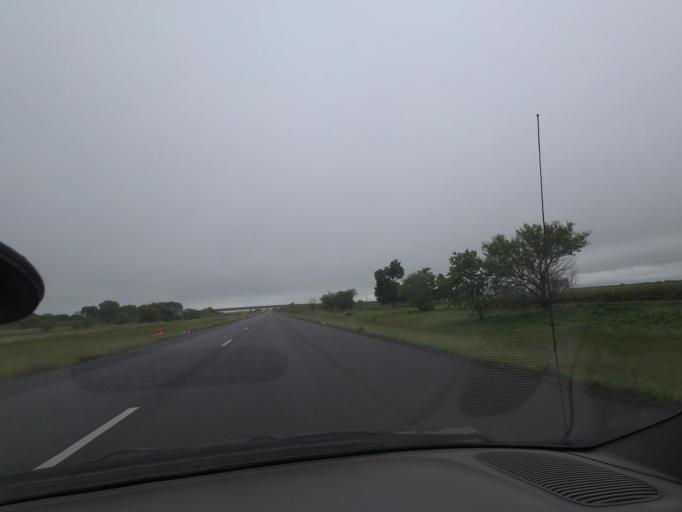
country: US
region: Illinois
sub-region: Macon County
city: Harristown
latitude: 39.8311
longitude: -89.1080
